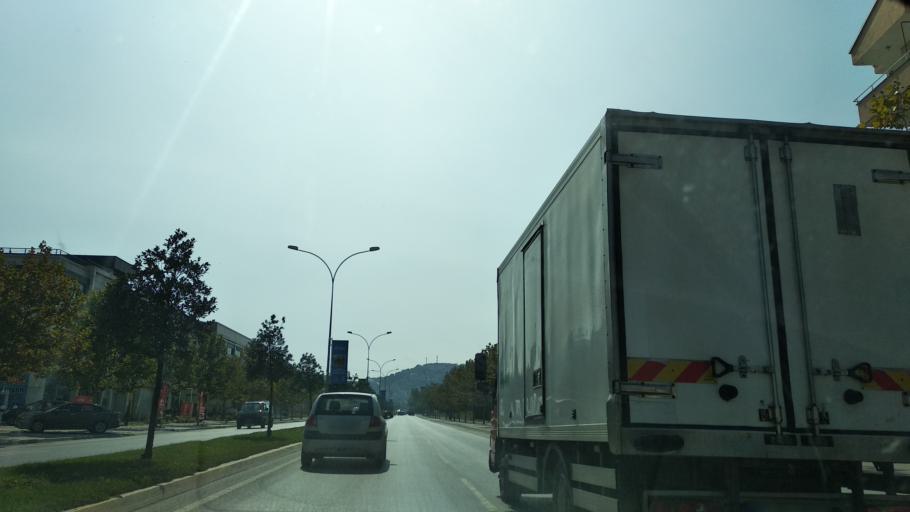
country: TR
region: Sakarya
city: Adapazari
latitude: 40.7703
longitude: 30.3641
